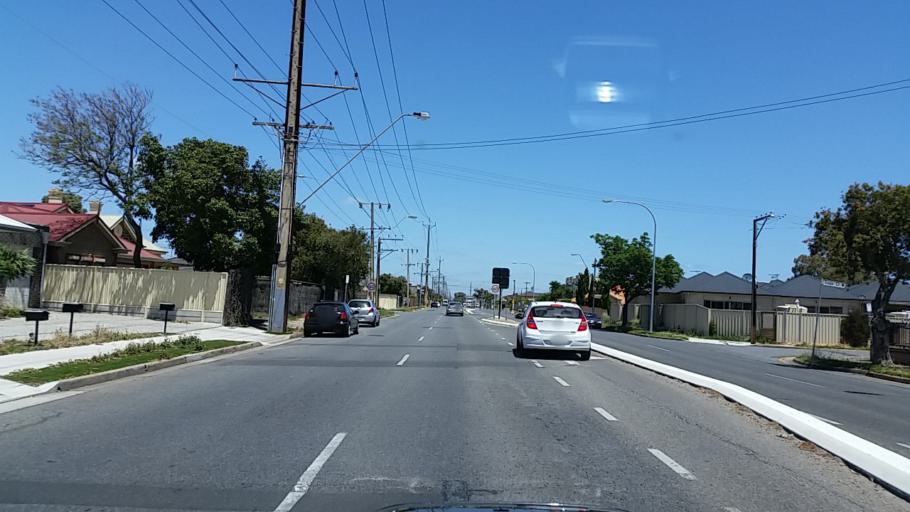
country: AU
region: South Australia
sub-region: Charles Sturt
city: Woodville West
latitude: -34.8865
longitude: 138.5313
